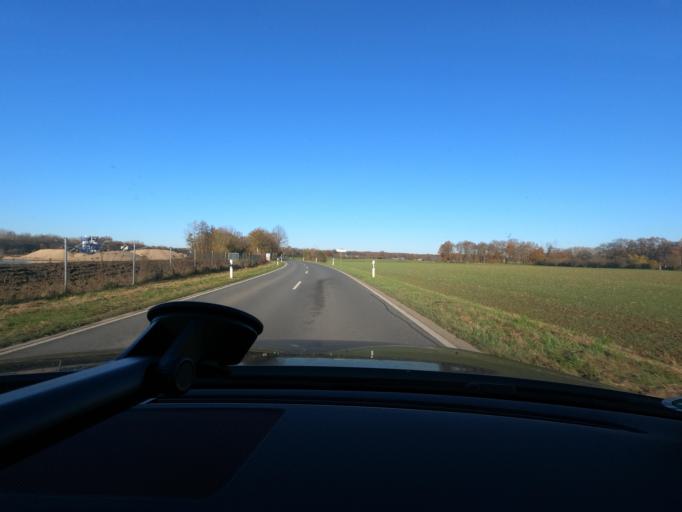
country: DE
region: North Rhine-Westphalia
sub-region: Regierungsbezirk Dusseldorf
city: Wachtendonk
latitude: 51.4349
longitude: 6.3455
